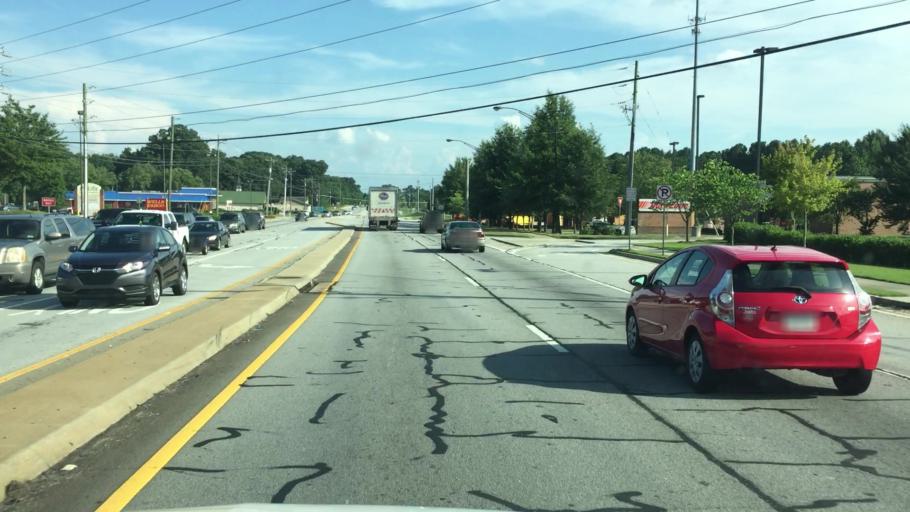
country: US
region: Georgia
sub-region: Gwinnett County
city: Snellville
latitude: 33.8035
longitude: -84.0430
